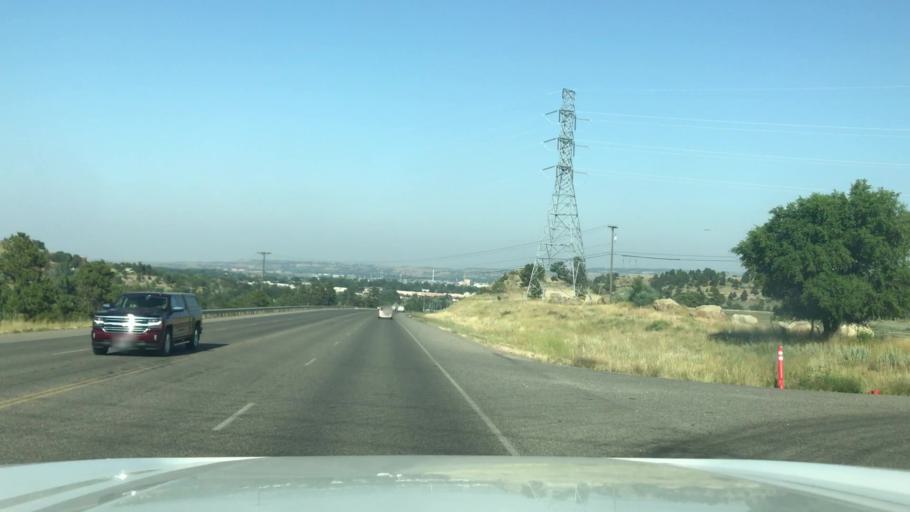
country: US
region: Montana
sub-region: Yellowstone County
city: Billings
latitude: 45.7998
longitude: -108.4976
